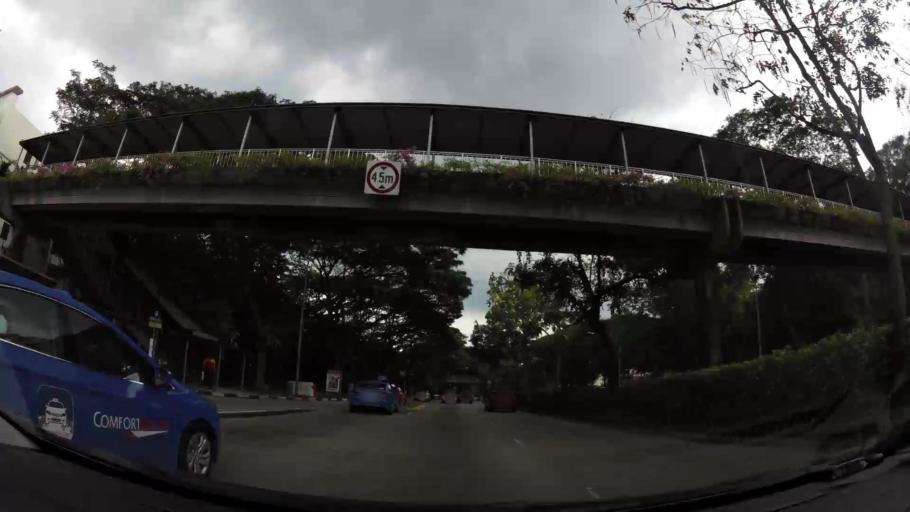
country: SG
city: Singapore
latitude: 1.3221
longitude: 103.8257
